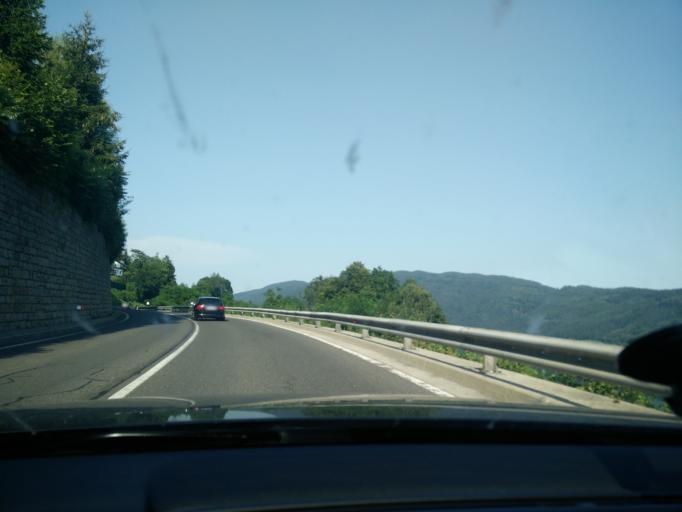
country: AT
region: Carinthia
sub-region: Politischer Bezirk Feldkirchen
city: Ossiach
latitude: 46.6675
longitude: 13.9339
